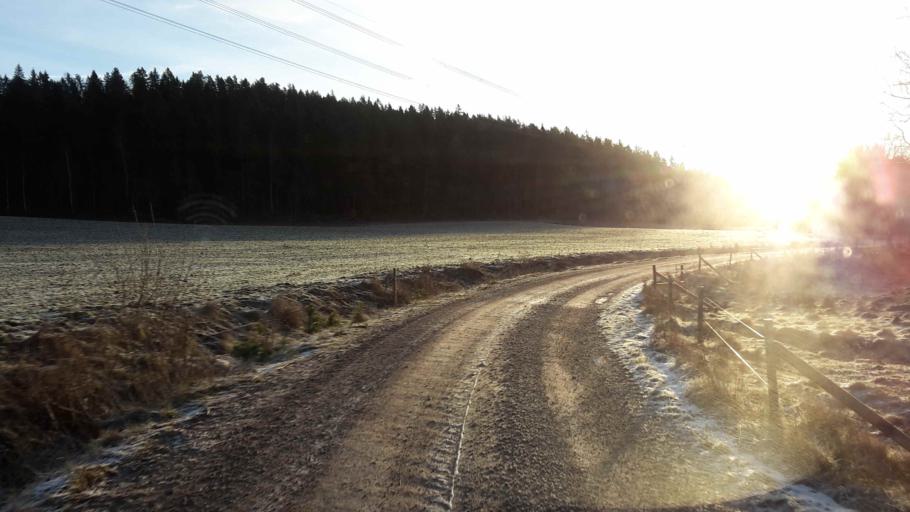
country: SE
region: OEstergoetland
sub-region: Atvidabergs Kommun
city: Atvidaberg
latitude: 58.2699
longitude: 16.1300
